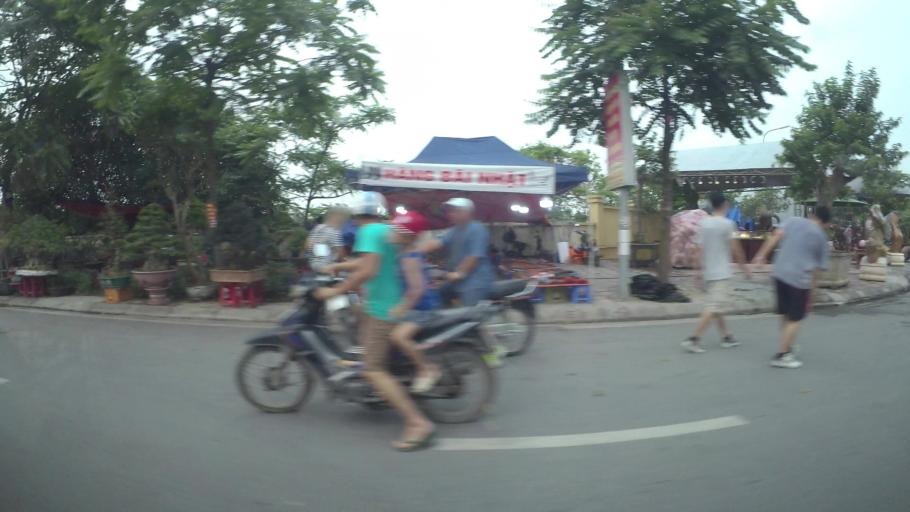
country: VN
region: Ha Noi
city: Hoan Kiem
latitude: 21.0537
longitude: 105.8930
